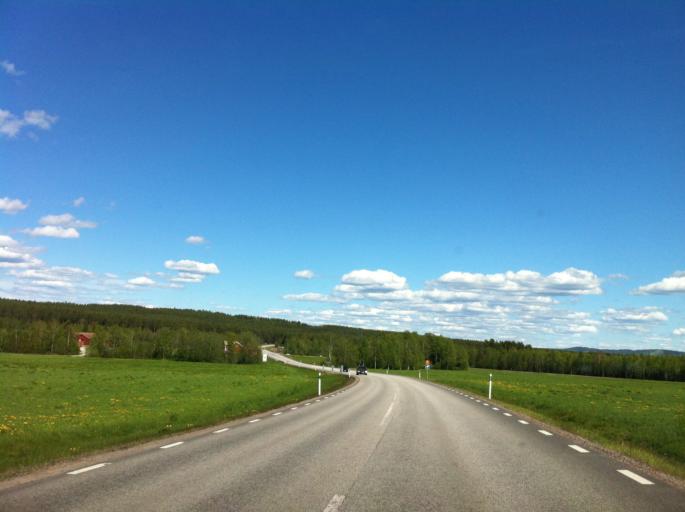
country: SE
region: Dalarna
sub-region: Rattviks Kommun
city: Vikarbyn
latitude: 60.9055
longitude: 14.9421
